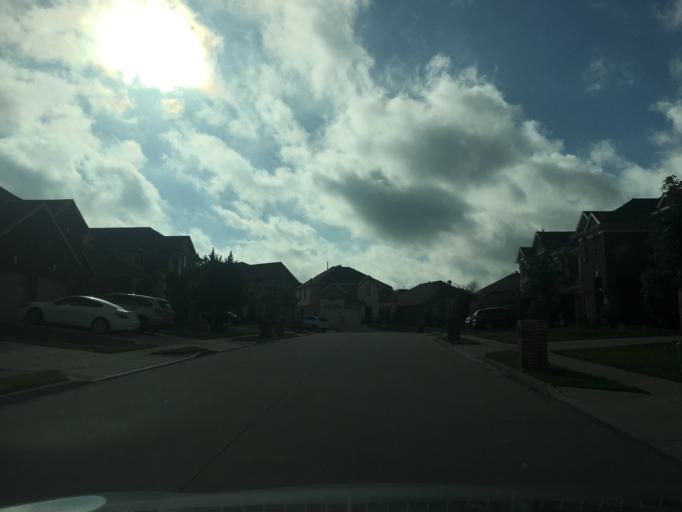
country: US
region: Texas
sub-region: Dallas County
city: Sachse
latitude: 32.9619
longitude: -96.5928
